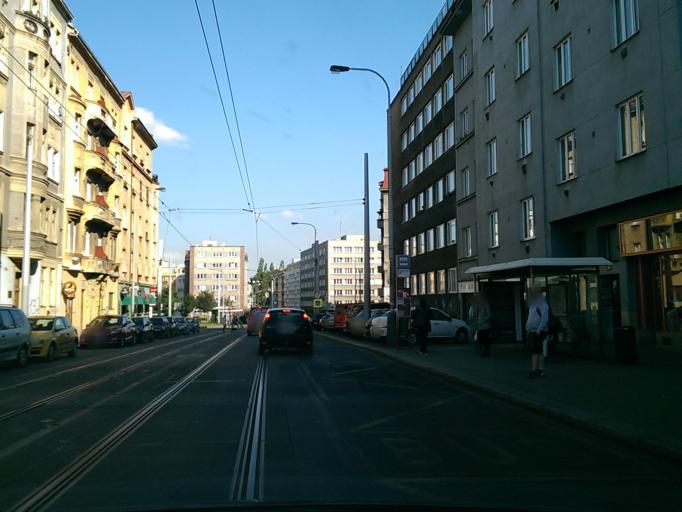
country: CZ
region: Praha
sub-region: Praha 2
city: Vysehrad
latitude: 50.0608
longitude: 14.4483
